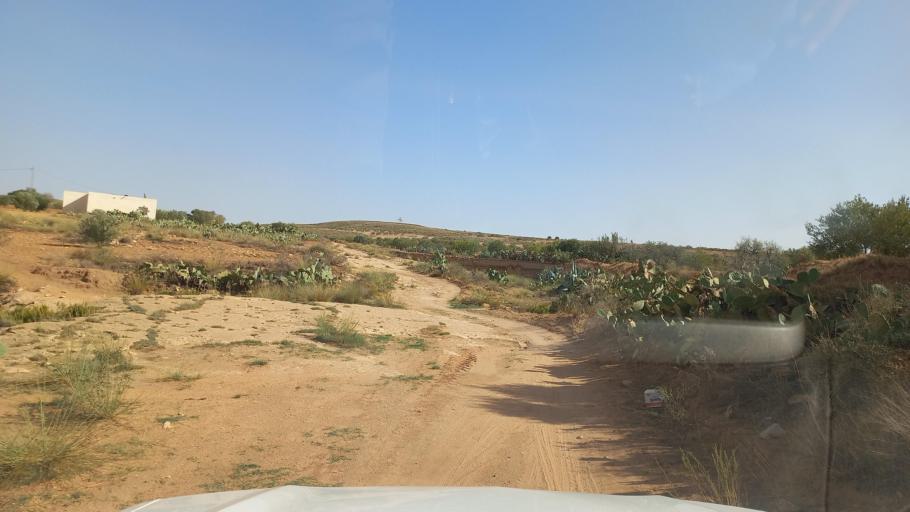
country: TN
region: Al Qasrayn
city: Kasserine
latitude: 35.2013
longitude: 8.9660
